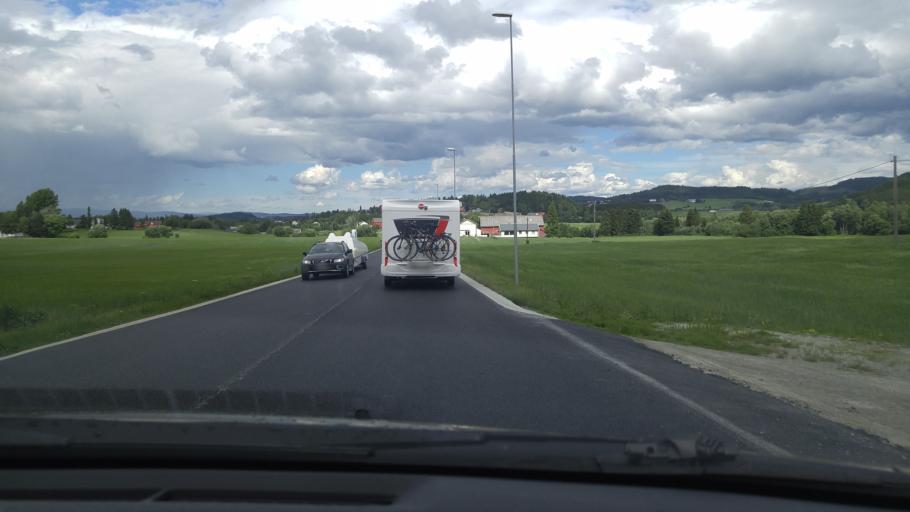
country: NO
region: Nord-Trondelag
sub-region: Steinkjer
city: Steinkjer
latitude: 63.9071
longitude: 11.4411
